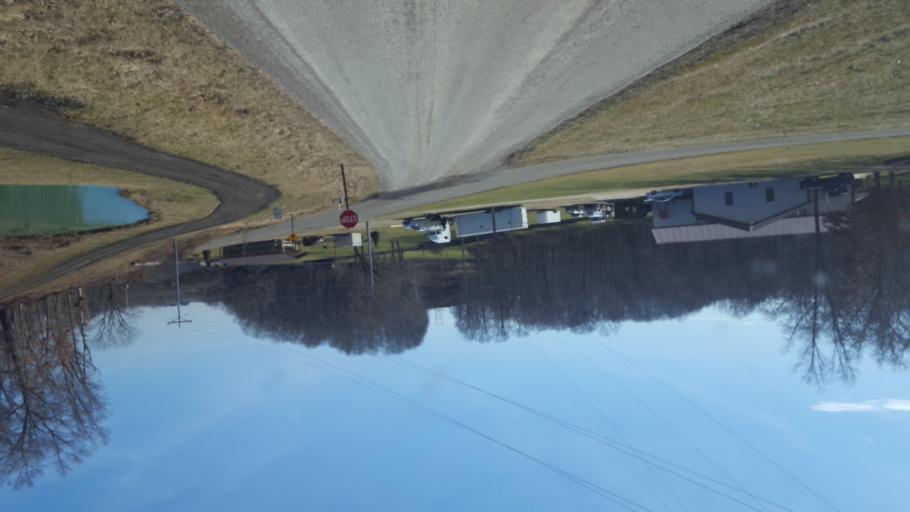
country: US
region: Ohio
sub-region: Knox County
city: Fredericktown
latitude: 40.5249
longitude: -82.4865
